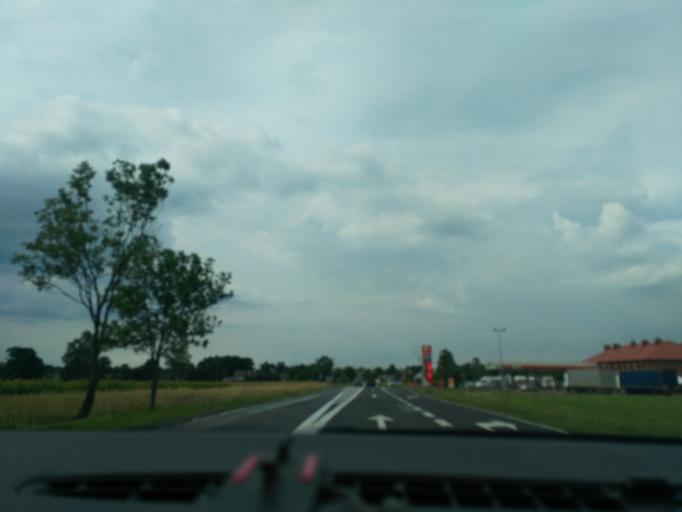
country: PL
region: Subcarpathian Voivodeship
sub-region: Powiat nizanski
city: Jezowe
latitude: 50.3677
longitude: 22.1254
